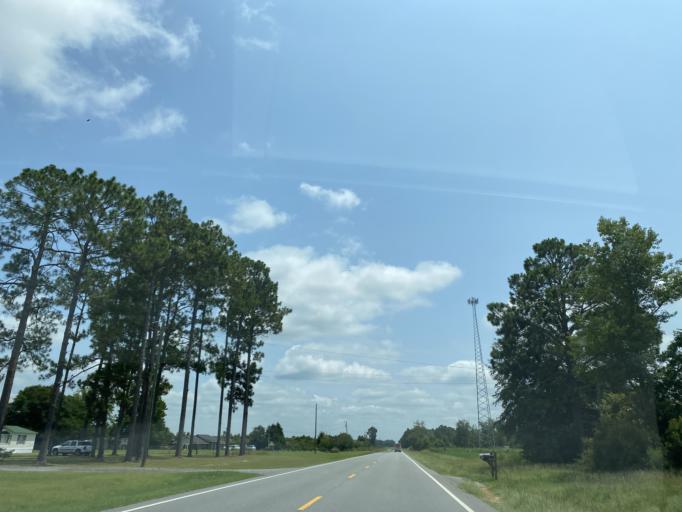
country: US
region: Georgia
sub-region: Jeff Davis County
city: Hazlehurst
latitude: 31.7309
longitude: -82.5326
